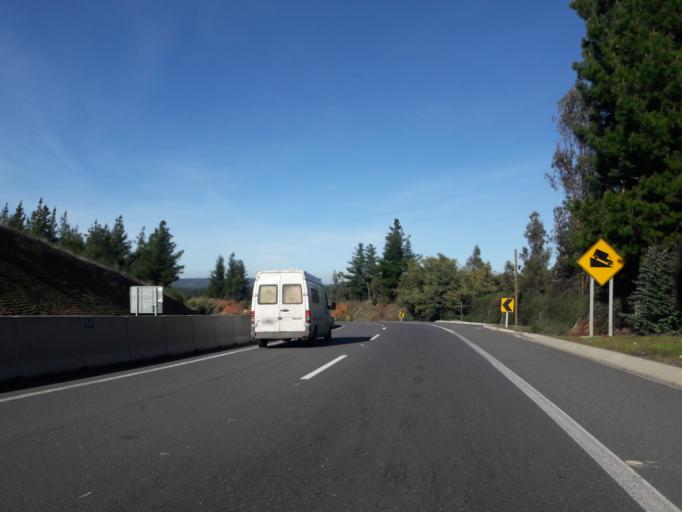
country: CL
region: Biobio
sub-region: Provincia de Biobio
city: Yumbel
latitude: -36.9767
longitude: -72.6516
